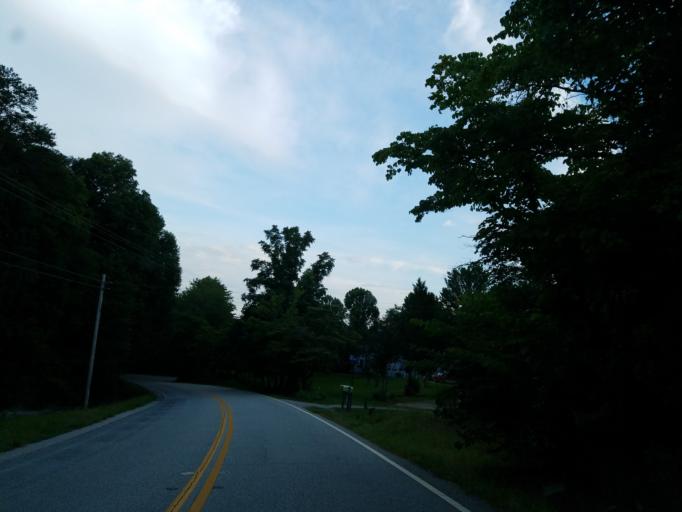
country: US
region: Georgia
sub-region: Lumpkin County
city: Dahlonega
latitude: 34.6009
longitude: -83.9702
